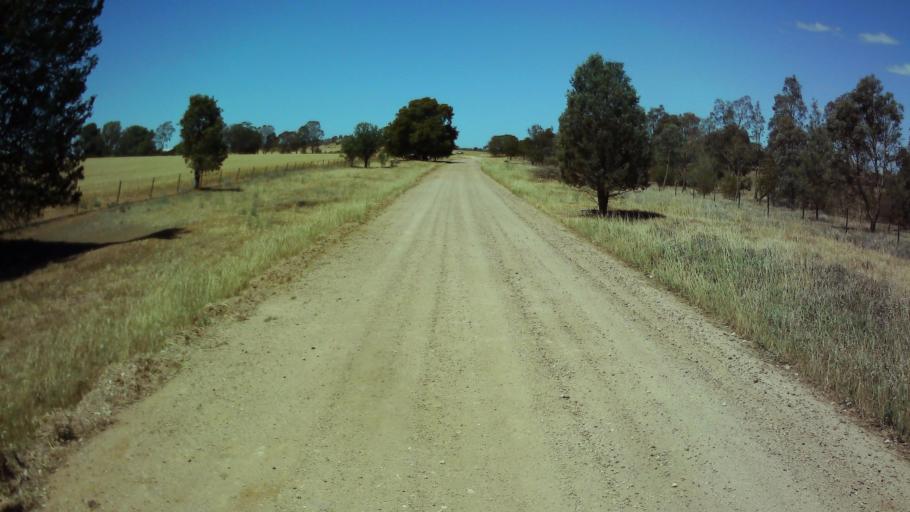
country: AU
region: New South Wales
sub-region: Weddin
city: Grenfell
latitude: -33.9564
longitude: 148.3290
